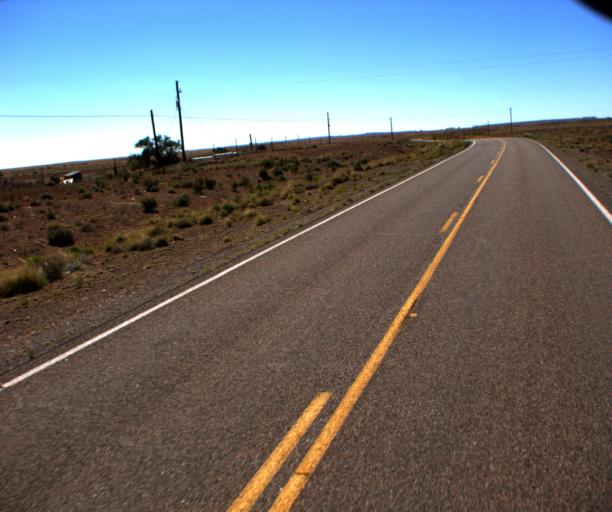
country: US
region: Arizona
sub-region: Coconino County
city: LeChee
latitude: 35.1558
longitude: -110.9043
